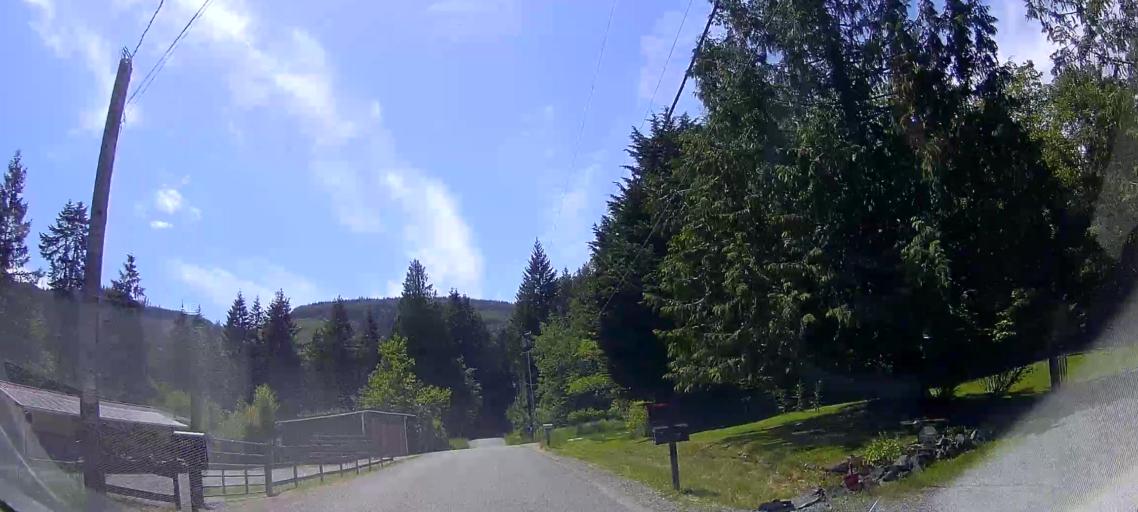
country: US
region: Washington
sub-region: Skagit County
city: Big Lake
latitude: 48.3776
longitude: -122.2589
